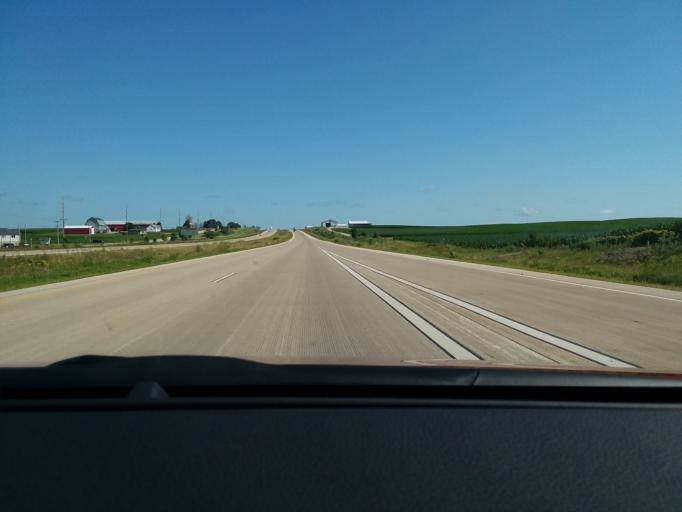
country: US
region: Wisconsin
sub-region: Dane County
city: Windsor
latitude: 43.2212
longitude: -89.3226
